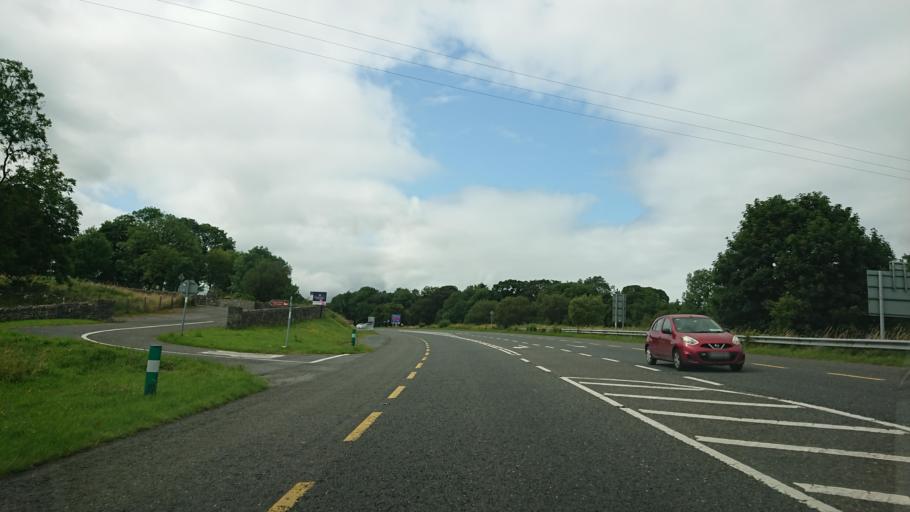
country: IE
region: Connaught
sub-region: Roscommon
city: Boyle
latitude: 53.9694
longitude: -8.2023
